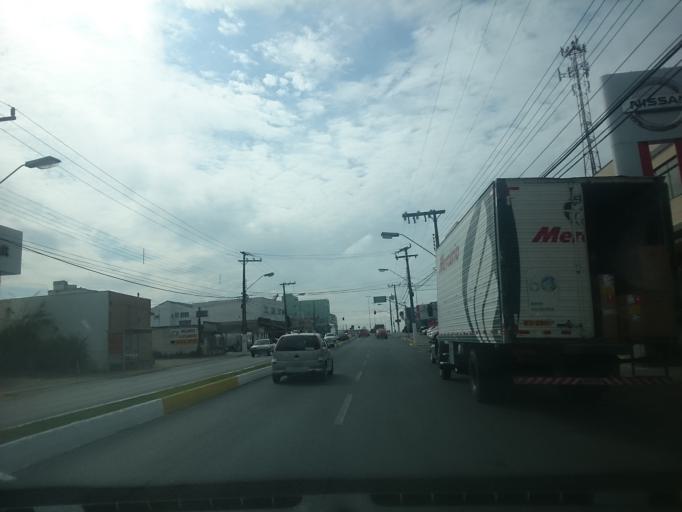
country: BR
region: Santa Catarina
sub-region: Lages
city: Lages
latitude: -27.8113
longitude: -50.3061
